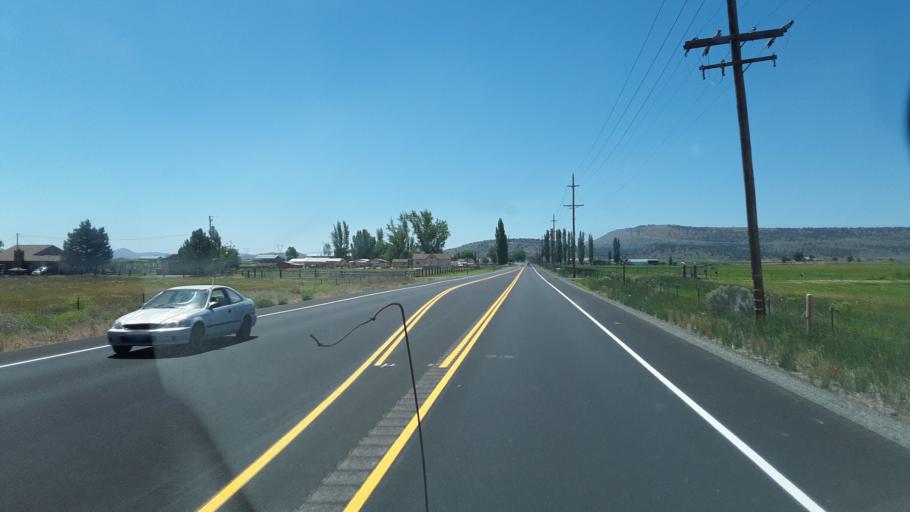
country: US
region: Oregon
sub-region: Klamath County
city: Altamont
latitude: 42.1110
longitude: -121.6986
